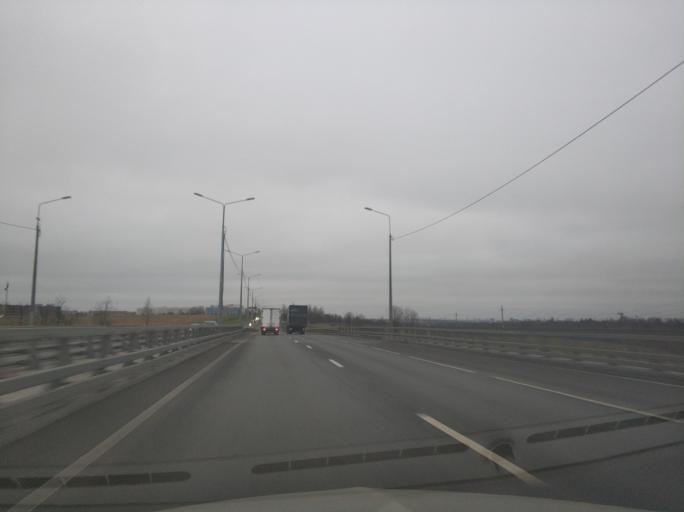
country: RU
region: St.-Petersburg
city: Pushkin
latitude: 59.7561
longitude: 30.3830
